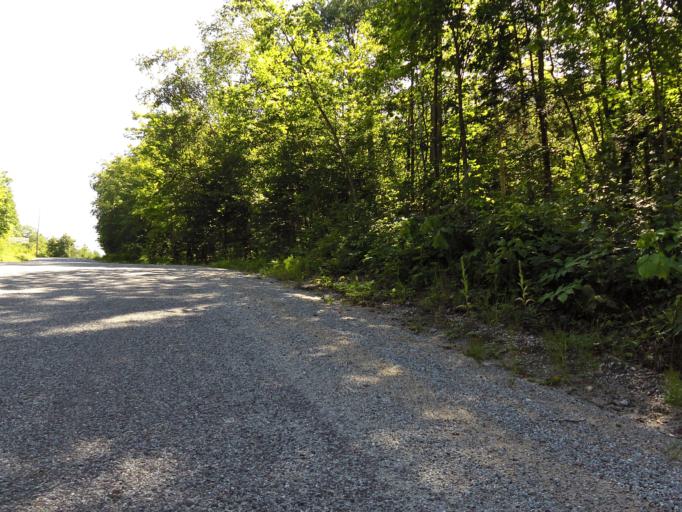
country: CA
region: Quebec
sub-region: Outaouais
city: Maniwaki
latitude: 46.2192
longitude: -76.1017
